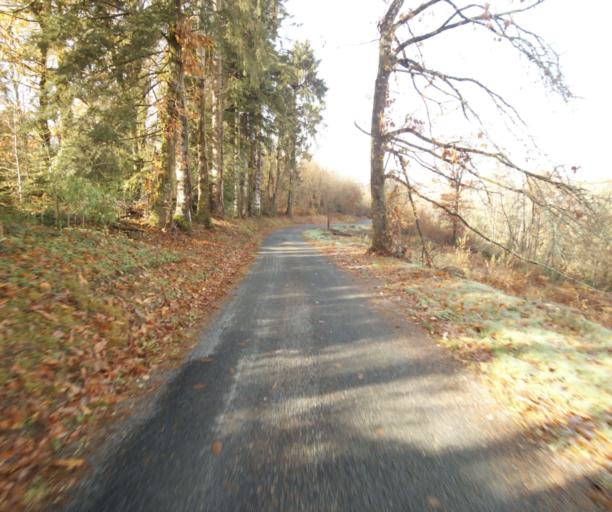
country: FR
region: Limousin
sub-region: Departement de la Correze
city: Chameyrat
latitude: 45.2258
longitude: 1.7347
